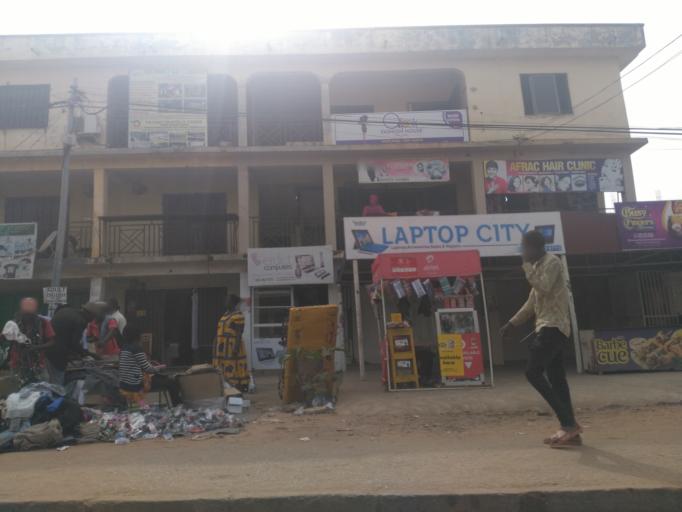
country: GH
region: Ashanti
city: Kumasi
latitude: 6.7060
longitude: -1.6358
